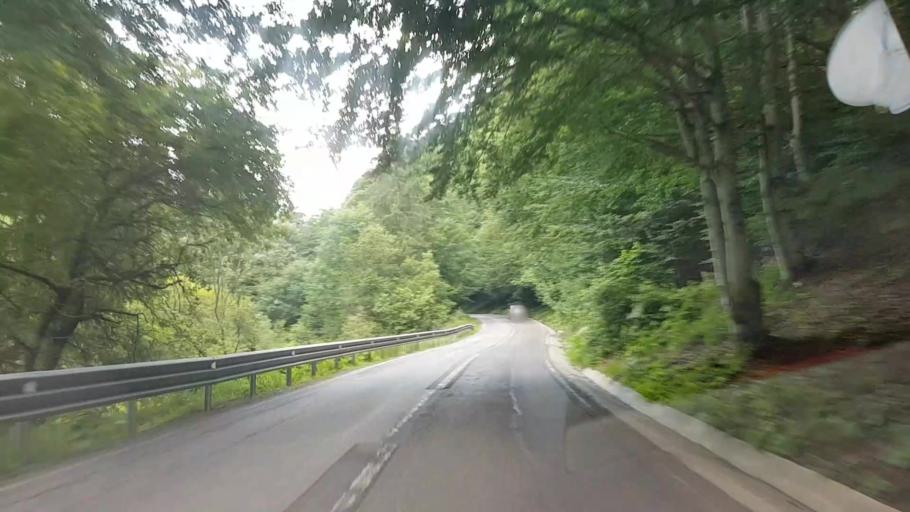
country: RO
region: Harghita
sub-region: Comuna Praid
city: Ocna de Sus
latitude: 46.6182
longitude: 25.2487
